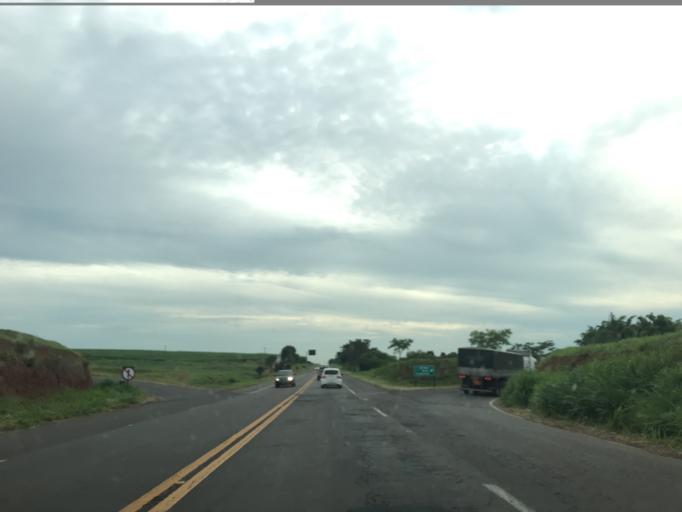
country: BR
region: Sao Paulo
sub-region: Birigui
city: Birigui
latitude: -21.5695
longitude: -50.4379
